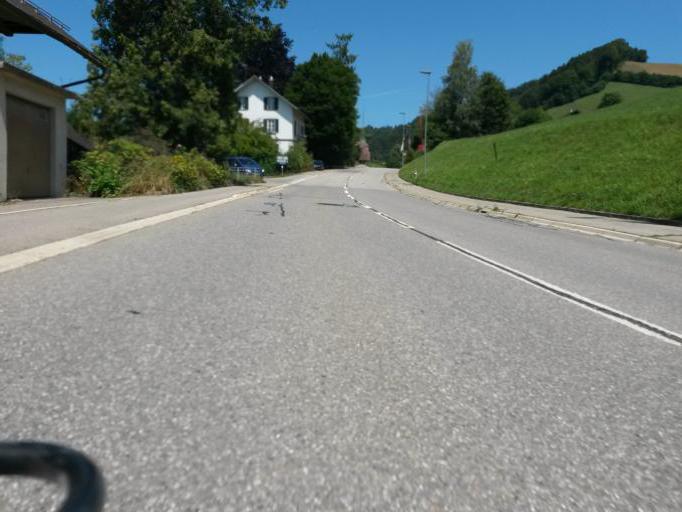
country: CH
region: Bern
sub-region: Bern-Mittelland District
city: Walkringen
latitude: 46.9451
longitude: 7.6185
